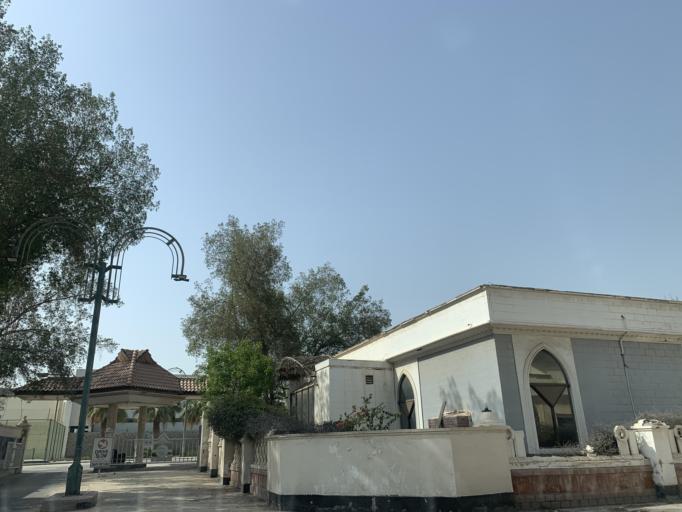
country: BH
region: Manama
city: Jidd Hafs
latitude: 26.2157
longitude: 50.5102
